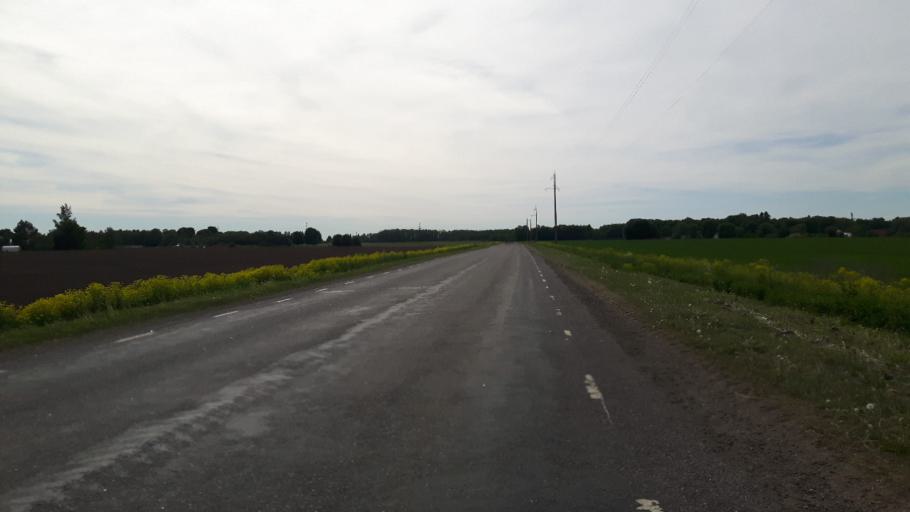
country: EE
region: Harju
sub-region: Maardu linn
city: Maardu
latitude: 59.4255
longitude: 25.0349
